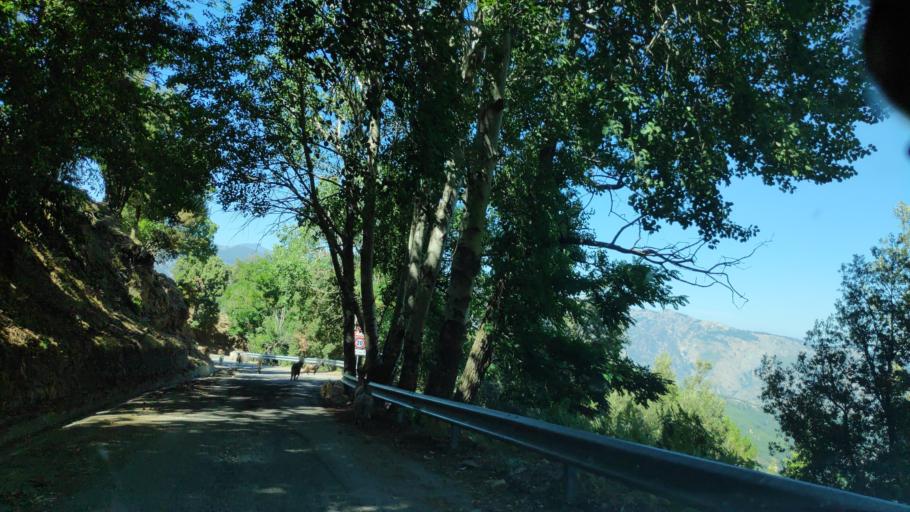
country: IT
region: Calabria
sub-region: Provincia di Reggio Calabria
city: Africo Vecchio
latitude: 38.0404
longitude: 15.9503
